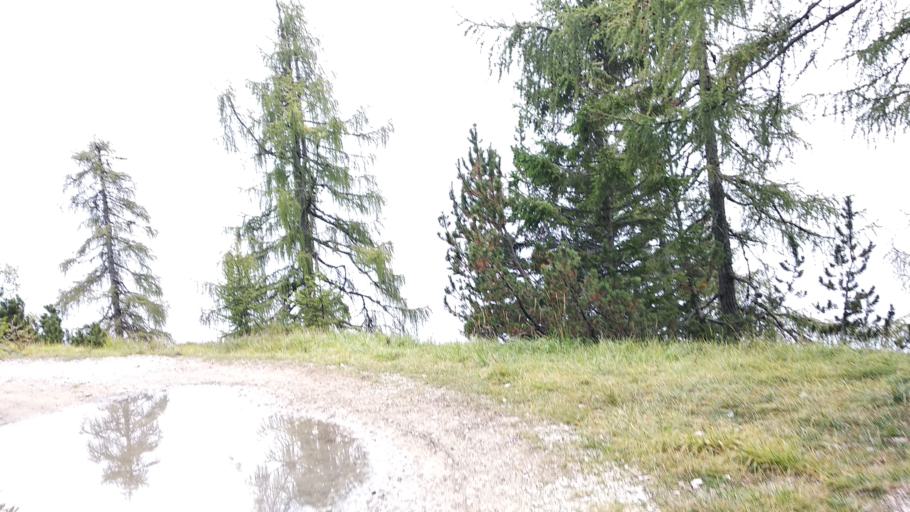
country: IT
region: Trentino-Alto Adige
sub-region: Provincia di Trento
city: Borgo
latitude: 45.9664
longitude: 11.4380
